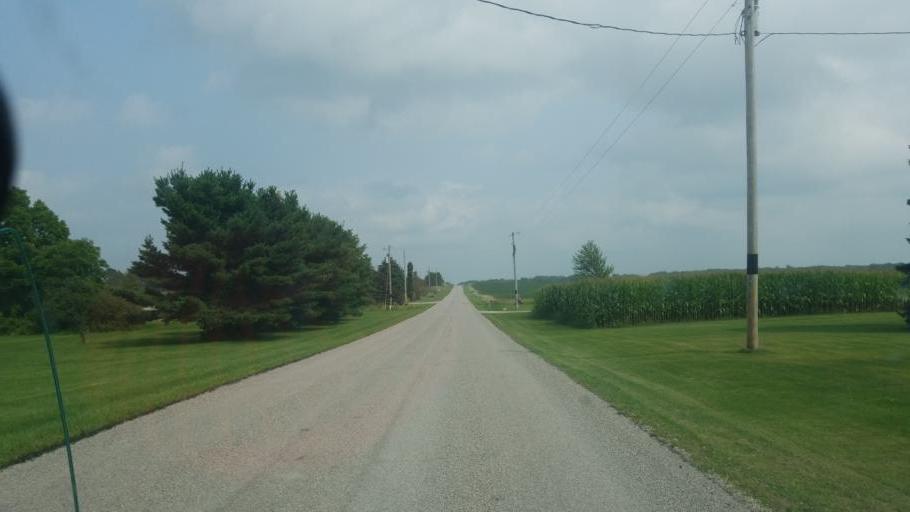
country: US
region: Ohio
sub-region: Huron County
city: Greenwich
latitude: 41.0669
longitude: -82.5557
